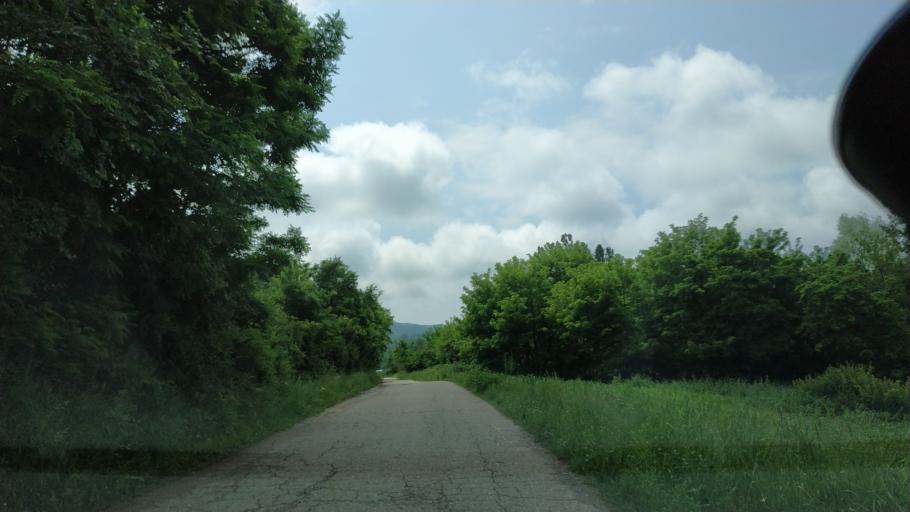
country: RS
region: Central Serbia
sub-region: Nisavski Okrug
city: Aleksinac
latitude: 43.4347
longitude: 21.7117
